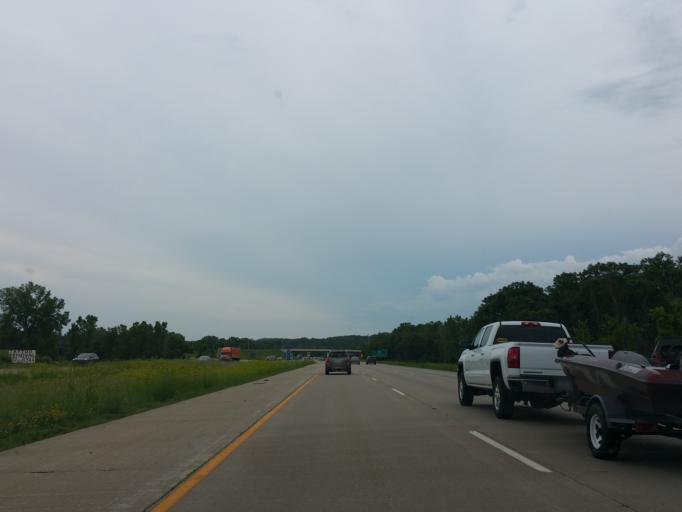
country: US
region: Wisconsin
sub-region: Columbia County
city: Poynette
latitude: 43.3978
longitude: -89.4671
